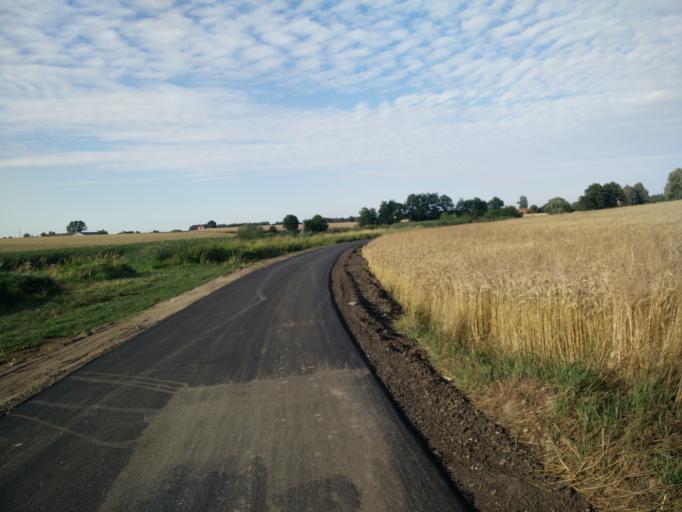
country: PL
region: Greater Poland Voivodeship
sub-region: Powiat sredzki
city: Sroda Wielkopolska
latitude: 52.2498
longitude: 17.3012
